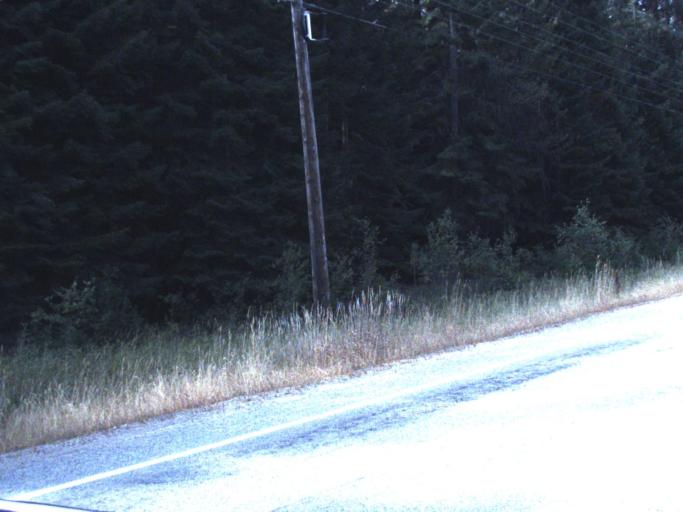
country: US
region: Washington
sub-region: Pend Oreille County
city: Newport
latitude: 48.2996
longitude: -117.2845
